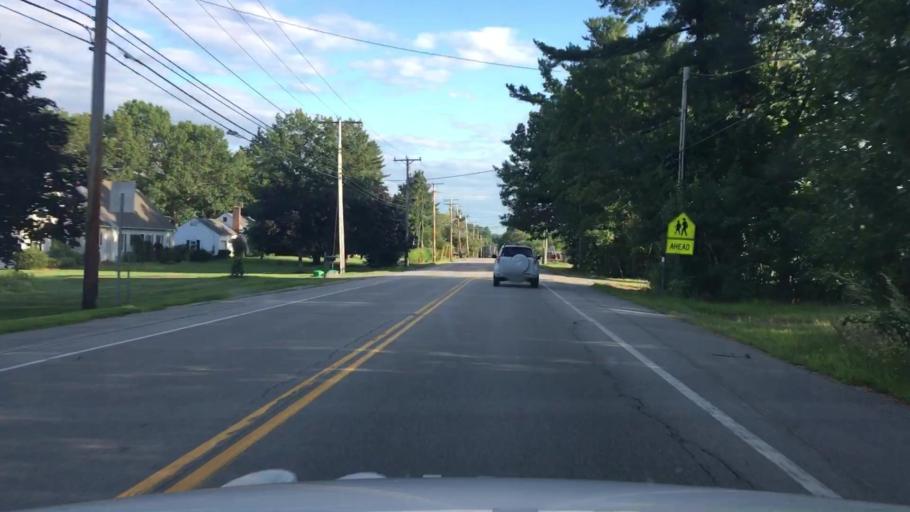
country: US
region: Maine
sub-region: York County
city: Eliot
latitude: 43.1540
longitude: -70.8406
